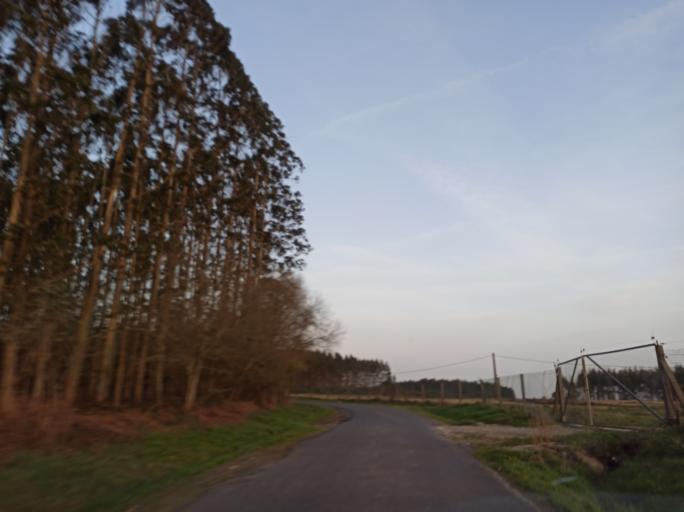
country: ES
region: Galicia
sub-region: Provincia da Coruna
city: Coiros
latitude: 43.1749
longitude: -8.1203
